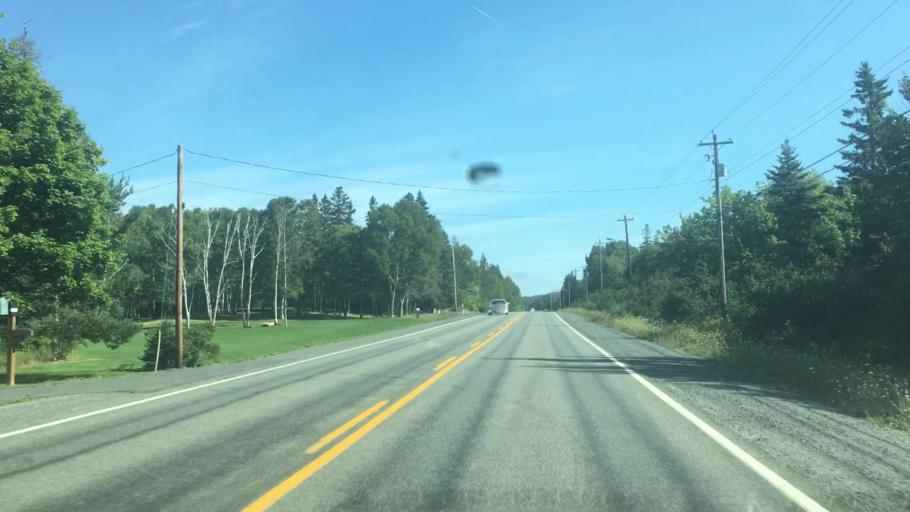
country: CA
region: Nova Scotia
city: Sydney
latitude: 45.9849
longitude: -60.4206
